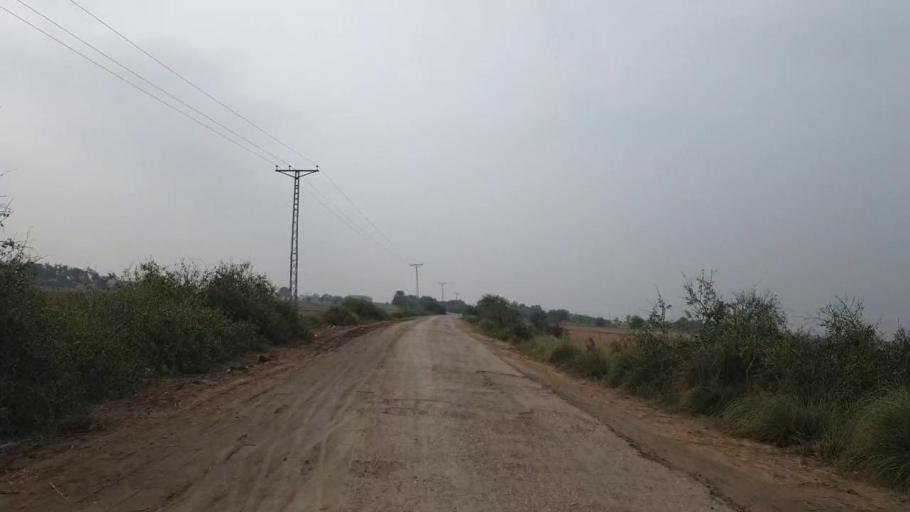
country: PK
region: Sindh
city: Matli
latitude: 24.9459
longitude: 68.5775
